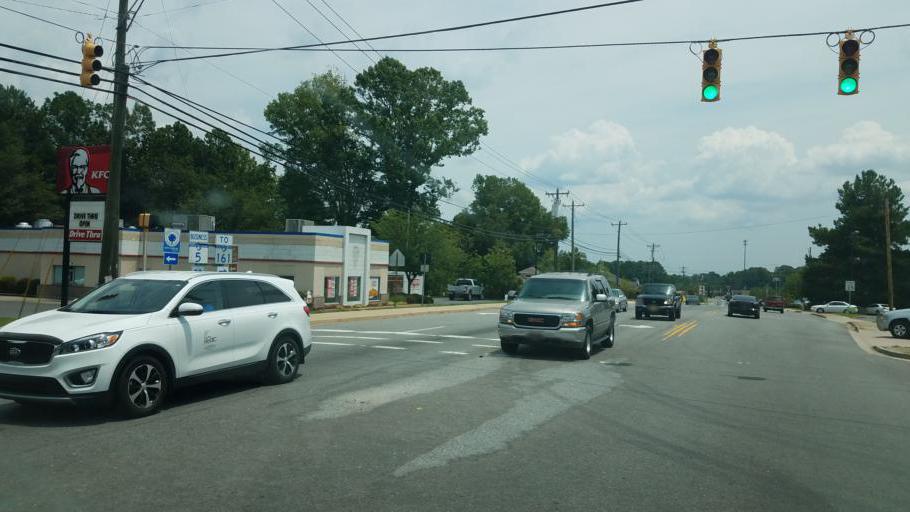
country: US
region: South Carolina
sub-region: York County
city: York
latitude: 34.9875
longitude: -81.2267
